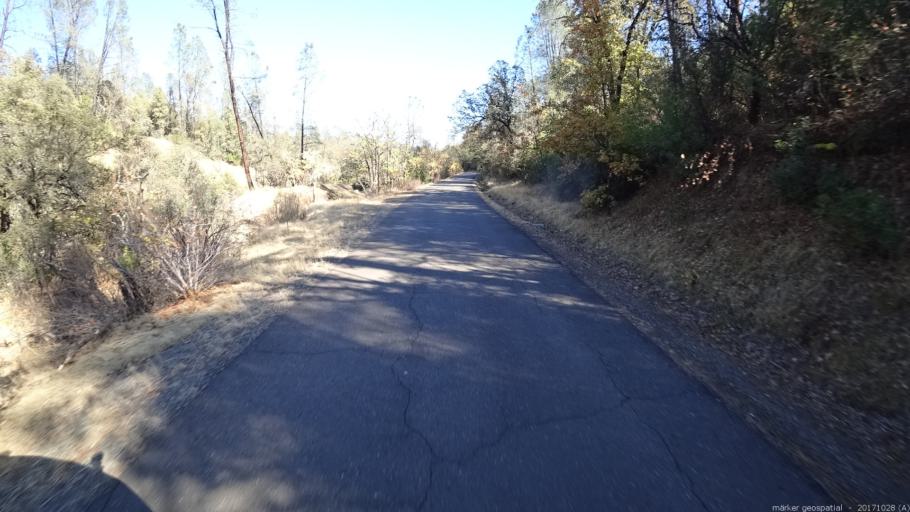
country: US
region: California
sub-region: Shasta County
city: Shasta
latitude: 40.5954
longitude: -122.4530
